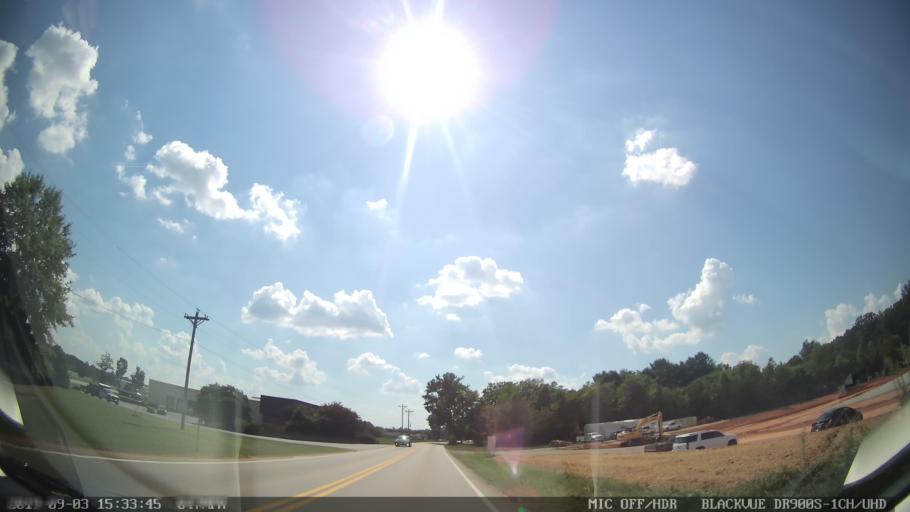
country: US
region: South Carolina
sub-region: Spartanburg County
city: Duncan
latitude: 34.8783
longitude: -82.1334
